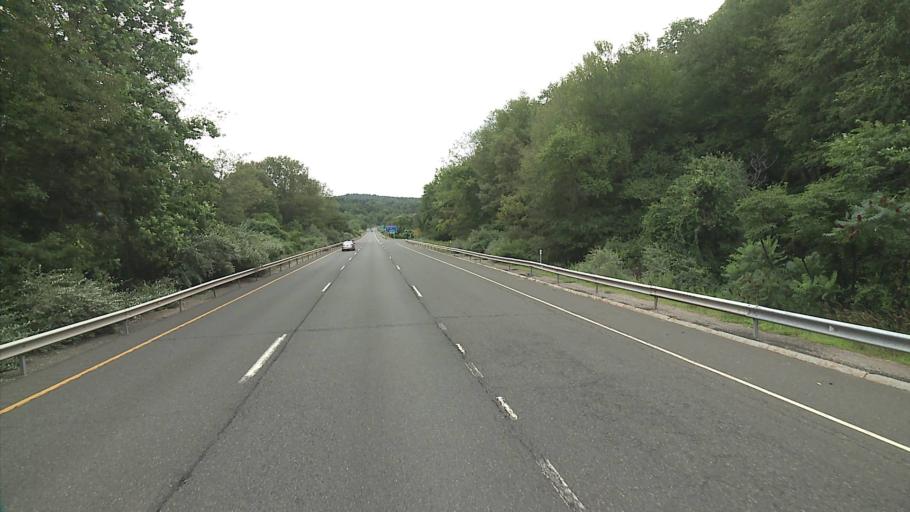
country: US
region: Connecticut
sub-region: Litchfield County
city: Thomaston
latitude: 41.6852
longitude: -73.0689
